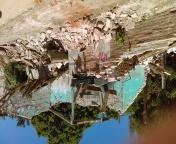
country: MX
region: Oaxaca
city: Asuncion Ixtaltepec
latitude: 16.5050
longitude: -95.0573
